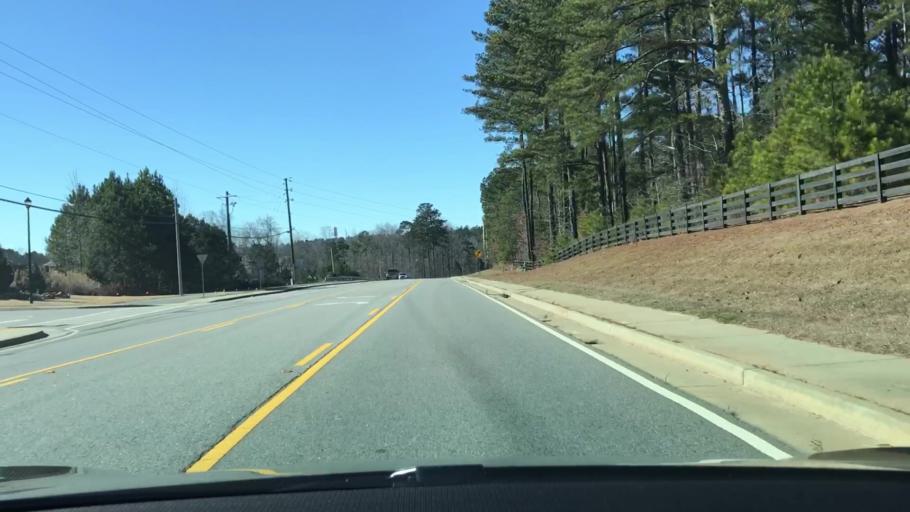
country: US
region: Georgia
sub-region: Forsyth County
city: Cumming
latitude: 34.1872
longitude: -84.1253
